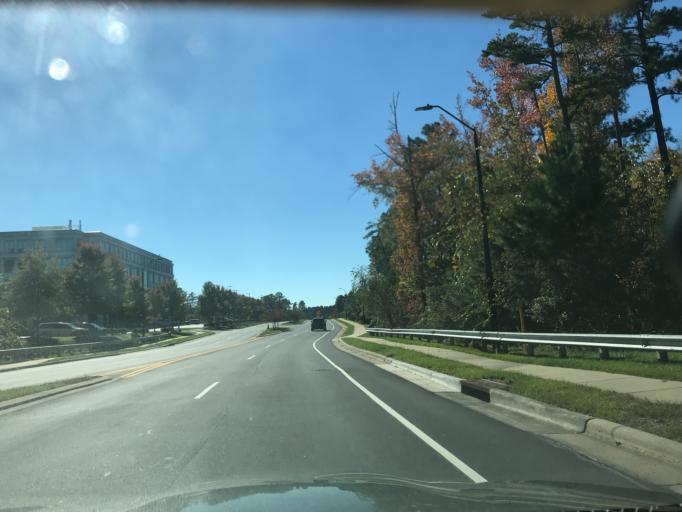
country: US
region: North Carolina
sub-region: Wake County
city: Morrisville
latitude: 35.9039
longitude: -78.7790
